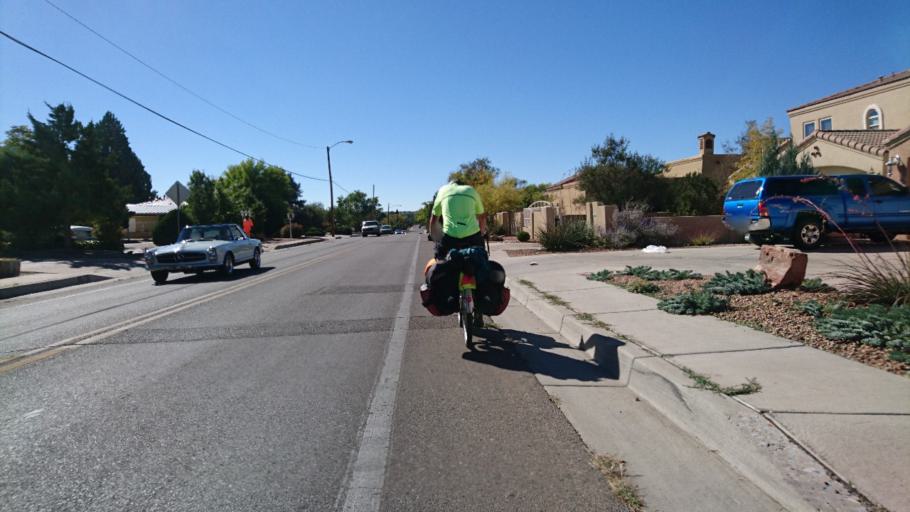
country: US
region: New Mexico
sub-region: Bernalillo County
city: Albuquerque
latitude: 35.0943
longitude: -106.5952
